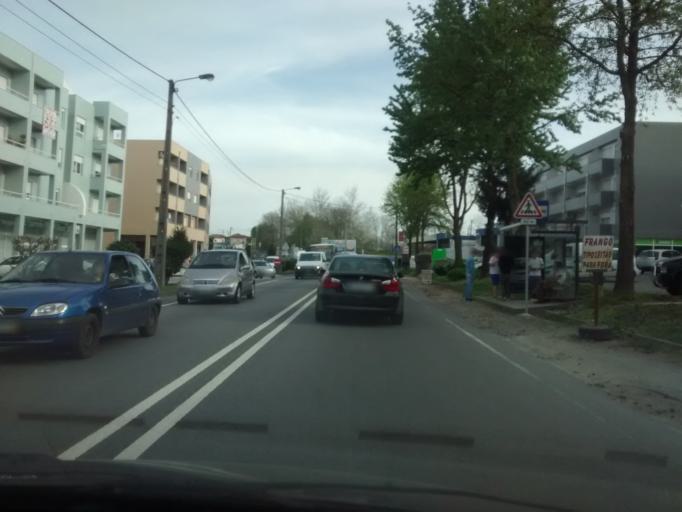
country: PT
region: Braga
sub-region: Guimaraes
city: Ponte
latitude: 41.4780
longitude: -8.3380
